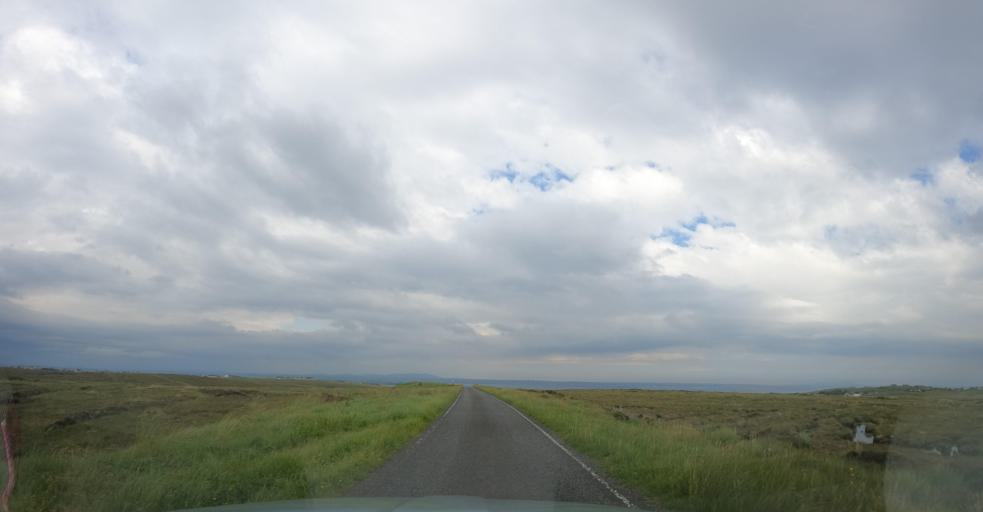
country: GB
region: Scotland
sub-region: Eilean Siar
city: Stornoway
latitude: 58.2037
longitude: -6.2425
